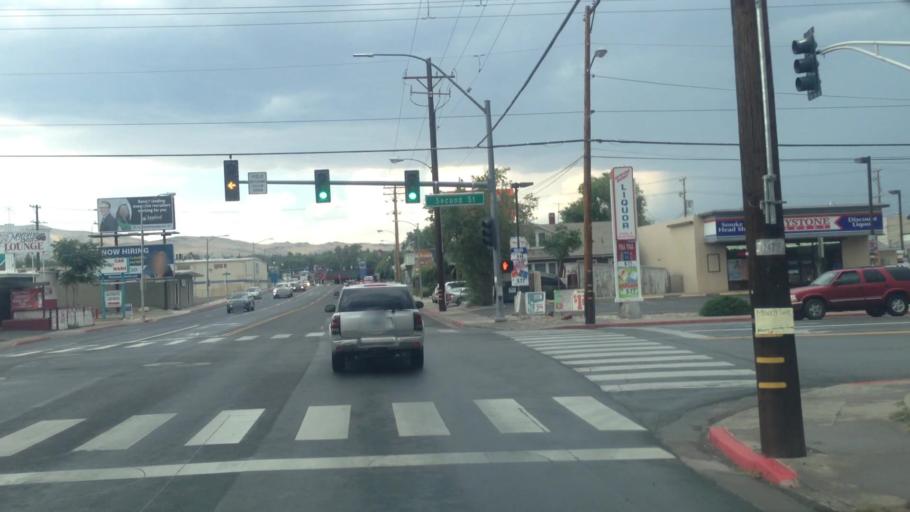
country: US
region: Nevada
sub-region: Washoe County
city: Reno
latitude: 39.5243
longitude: -119.8256
